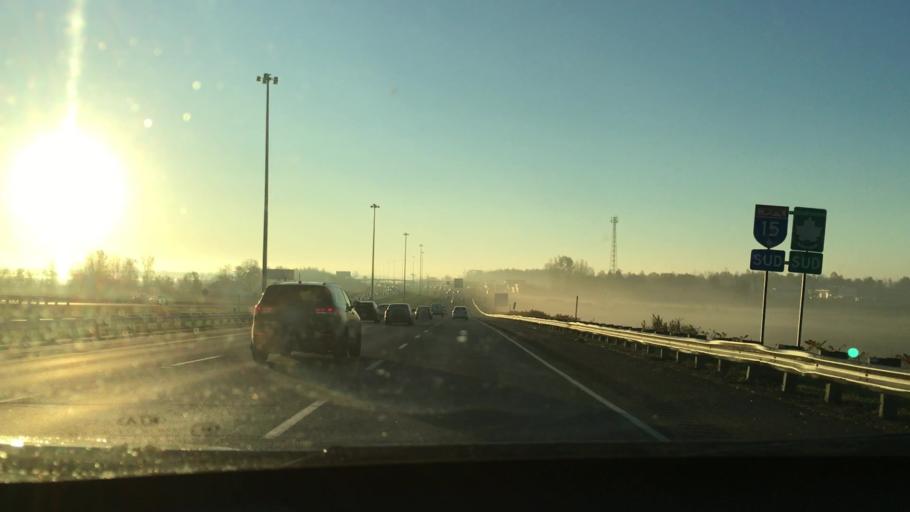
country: CA
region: Quebec
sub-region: Laurentides
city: Saint-Jerome
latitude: 45.7442
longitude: -74.0018
